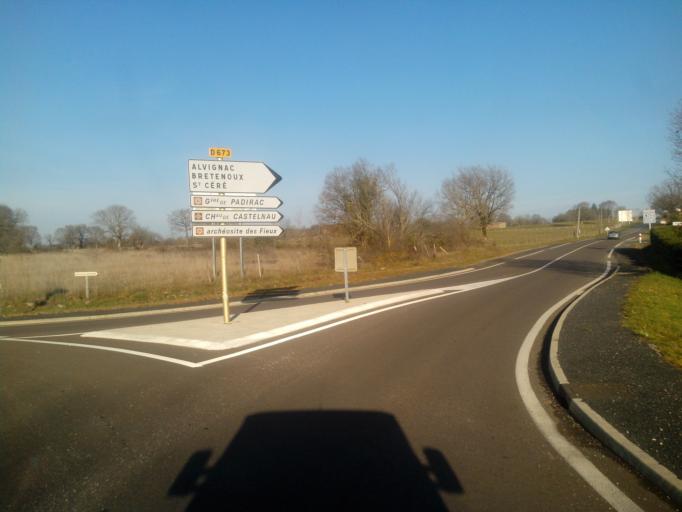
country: FR
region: Midi-Pyrenees
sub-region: Departement du Lot
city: Gramat
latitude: 44.8221
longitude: 1.6601
